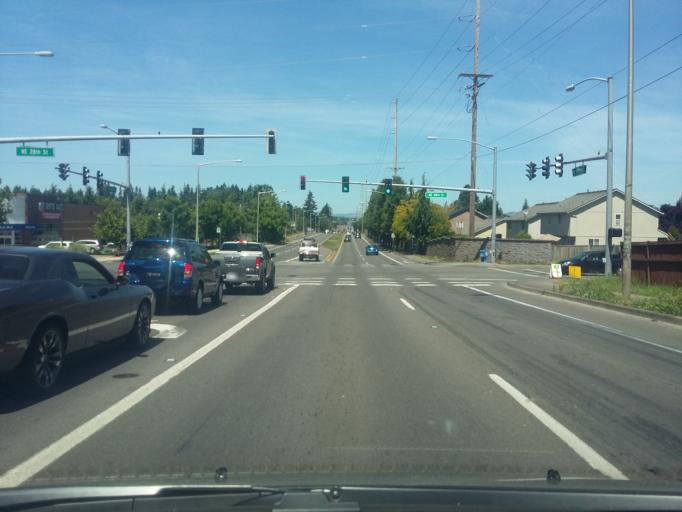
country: US
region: Washington
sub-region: Clark County
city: Mill Plain
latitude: 45.6424
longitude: -122.5060
